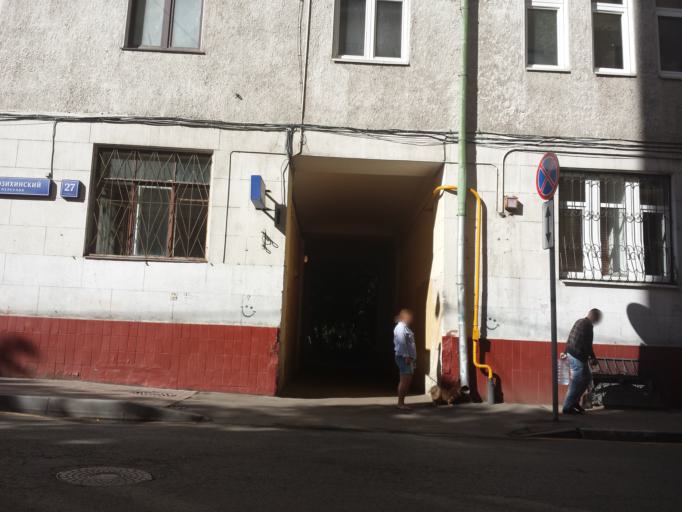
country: RU
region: Moscow
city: Moscow
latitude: 55.7652
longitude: 37.5945
